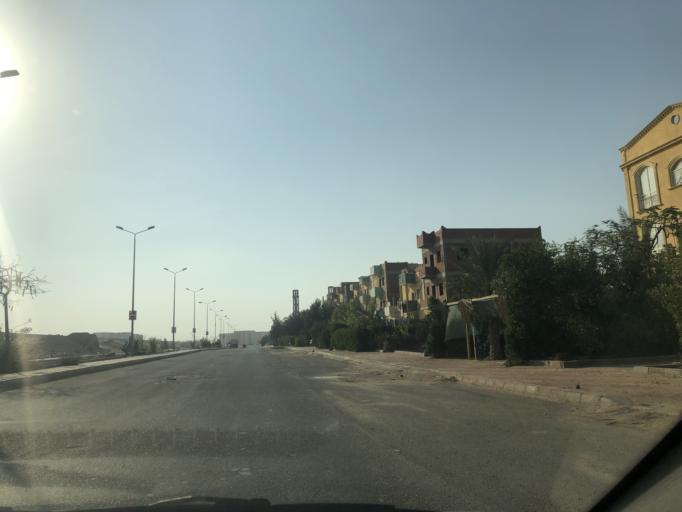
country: EG
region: Al Jizah
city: Madinat Sittah Uktubar
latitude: 29.9038
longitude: 30.9300
